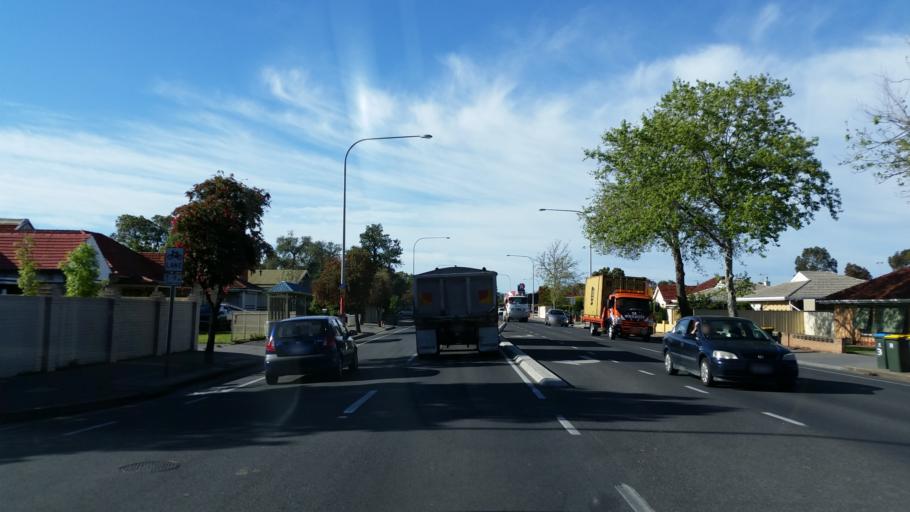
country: AU
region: South Australia
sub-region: Port Adelaide Enfield
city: Klemzig
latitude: -34.8747
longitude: 138.6194
